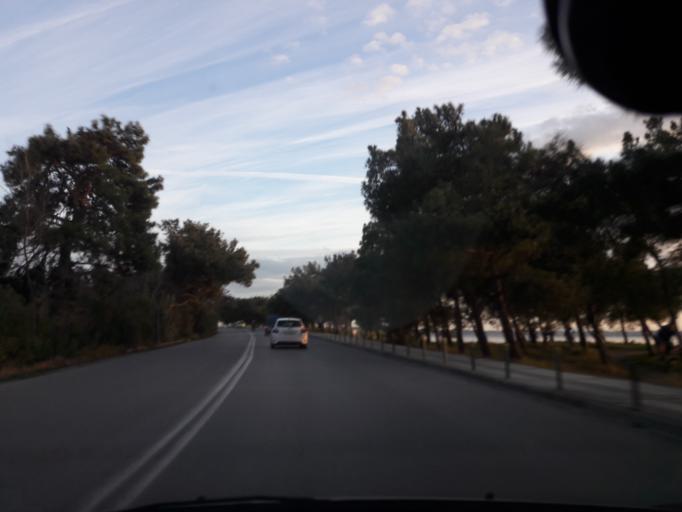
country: GR
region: Central Macedonia
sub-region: Nomos Thessalonikis
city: Kalamaria
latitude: 40.5824
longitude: 22.9370
